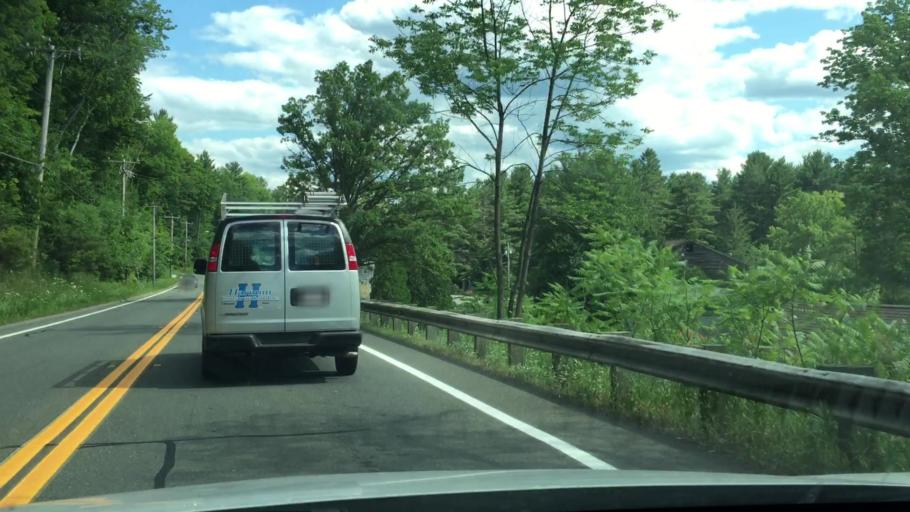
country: US
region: Massachusetts
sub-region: Berkshire County
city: Lee
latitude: 42.3227
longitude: -73.2602
